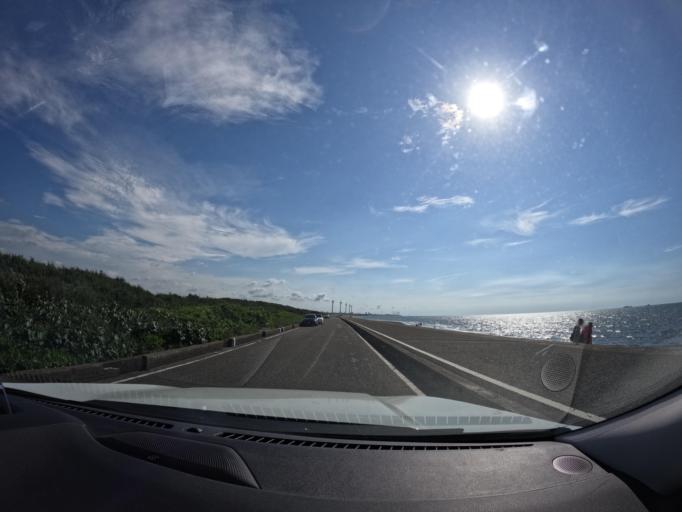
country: TW
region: Taiwan
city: Taoyuan City
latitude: 25.0903
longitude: 121.1783
